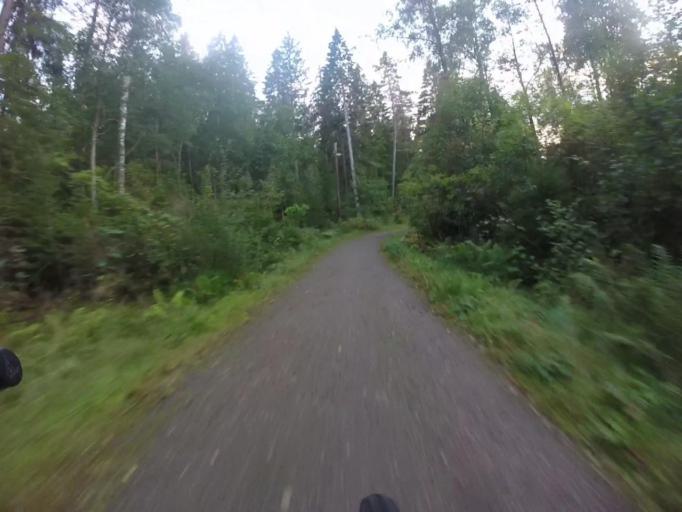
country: SE
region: Vaestra Goetaland
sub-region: Trollhattan
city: Trollhattan
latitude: 58.2990
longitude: 12.2585
